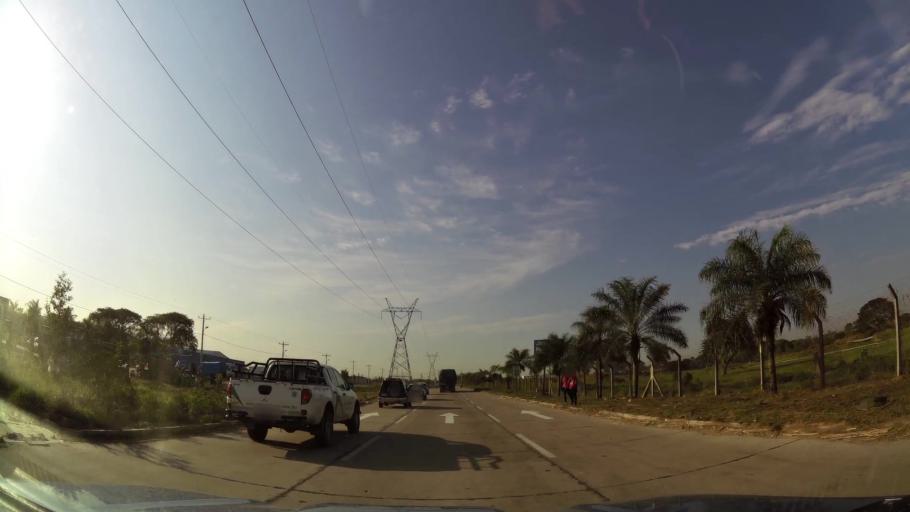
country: BO
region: Santa Cruz
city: Santa Cruz de la Sierra
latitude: -17.7001
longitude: -63.1331
